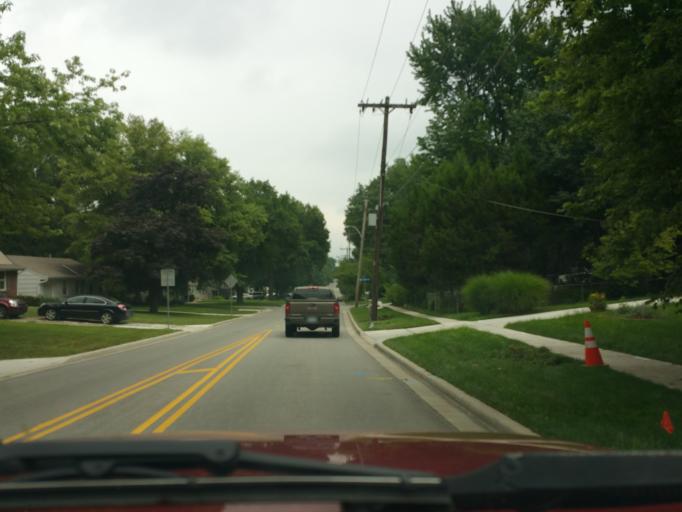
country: US
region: Kansas
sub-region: Johnson County
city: Fairway
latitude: 39.0150
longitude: -94.6391
